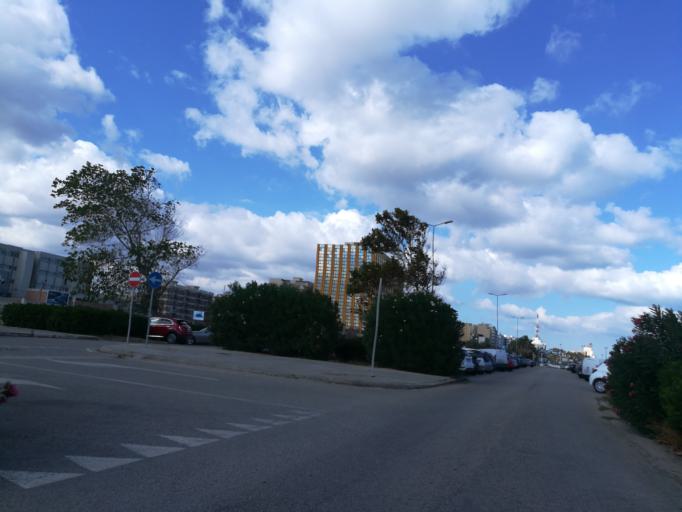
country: IT
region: Apulia
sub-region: Provincia di Bari
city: Bari
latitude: 41.1168
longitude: 16.8972
